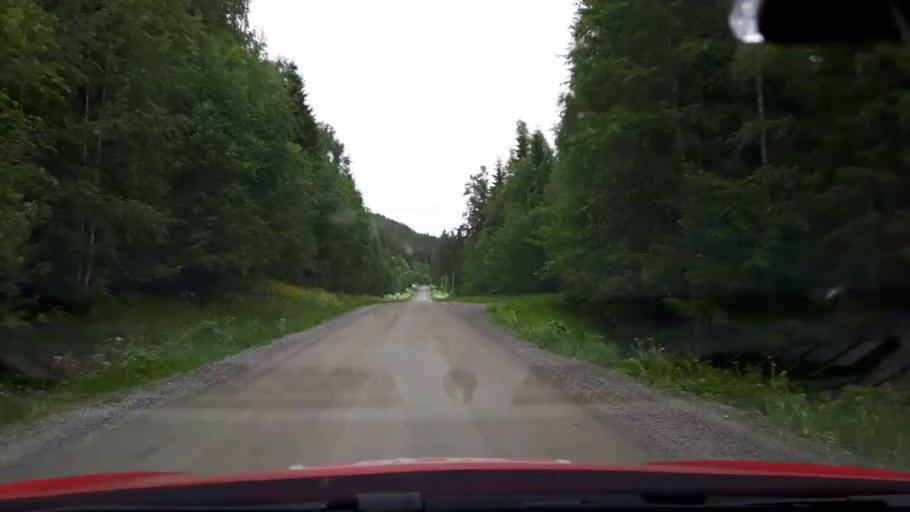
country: SE
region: Jaemtland
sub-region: Ragunda Kommun
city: Hammarstrand
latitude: 63.1802
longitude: 16.1753
